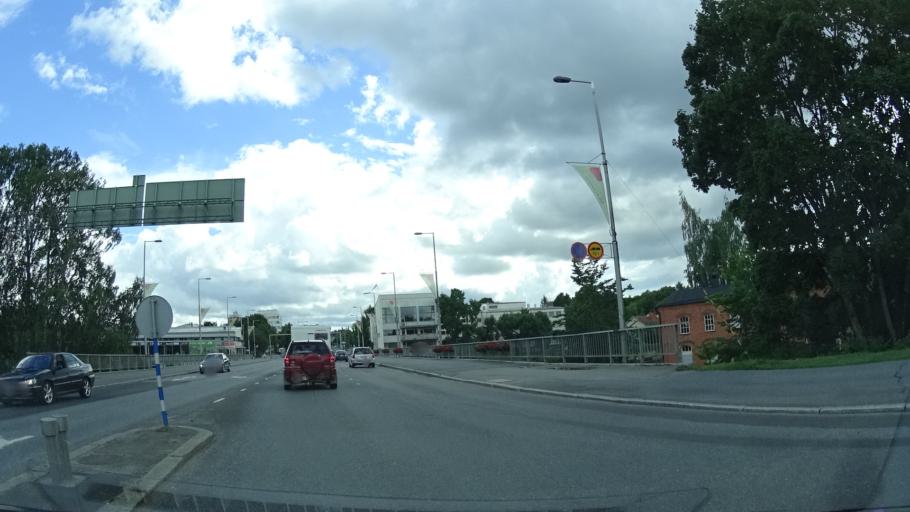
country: FI
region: Pirkanmaa
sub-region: Etelae-Pirkanmaa
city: Valkeakoski
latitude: 61.2656
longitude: 24.0306
